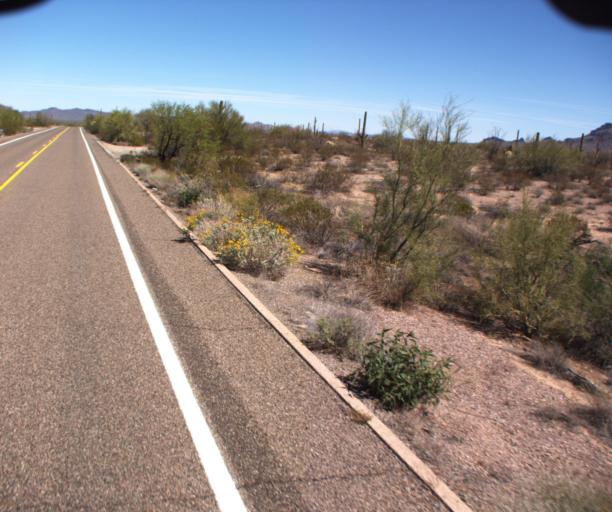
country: MX
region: Sonora
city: Sonoyta
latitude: 32.0916
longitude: -112.7746
